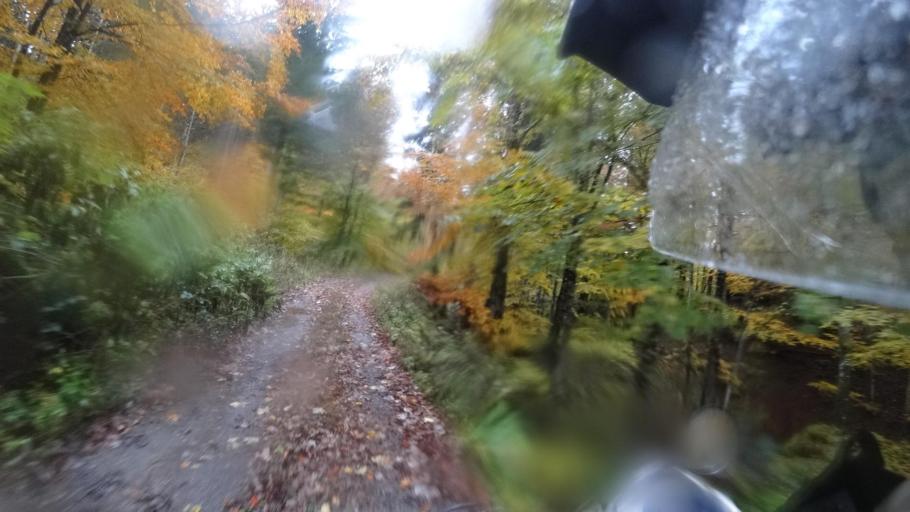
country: HR
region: Primorsko-Goranska
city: Vrbovsko
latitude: 45.3481
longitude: 15.0691
